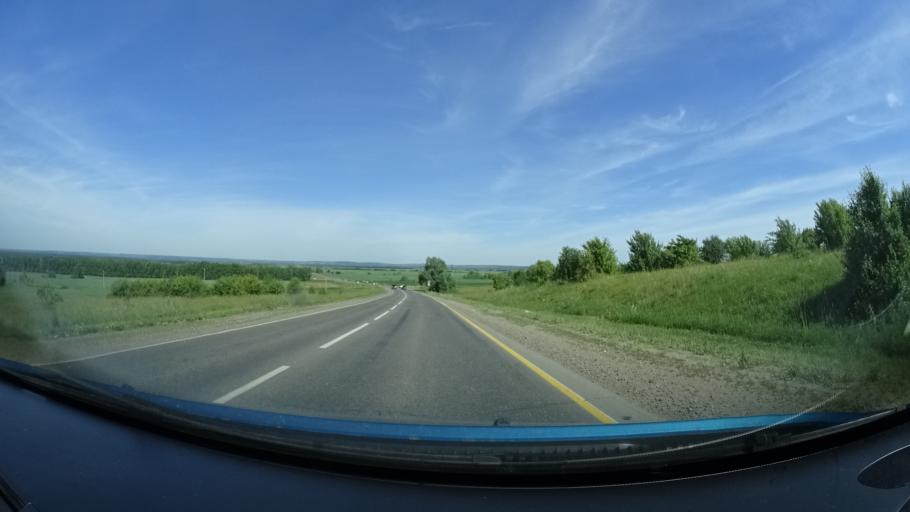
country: RU
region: Bashkortostan
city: Blagoveshchensk
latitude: 55.1808
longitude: 55.8527
